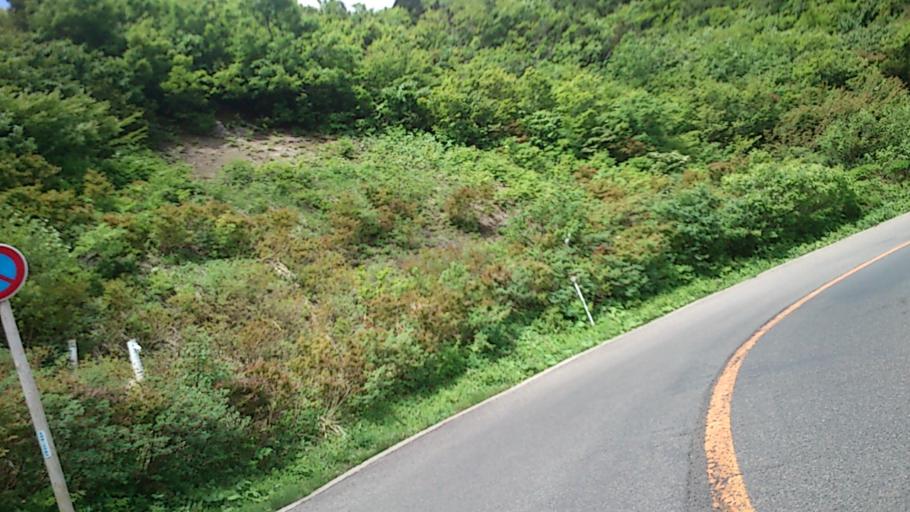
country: JP
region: Yamagata
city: Yamagata-shi
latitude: 38.1268
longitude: 140.4543
